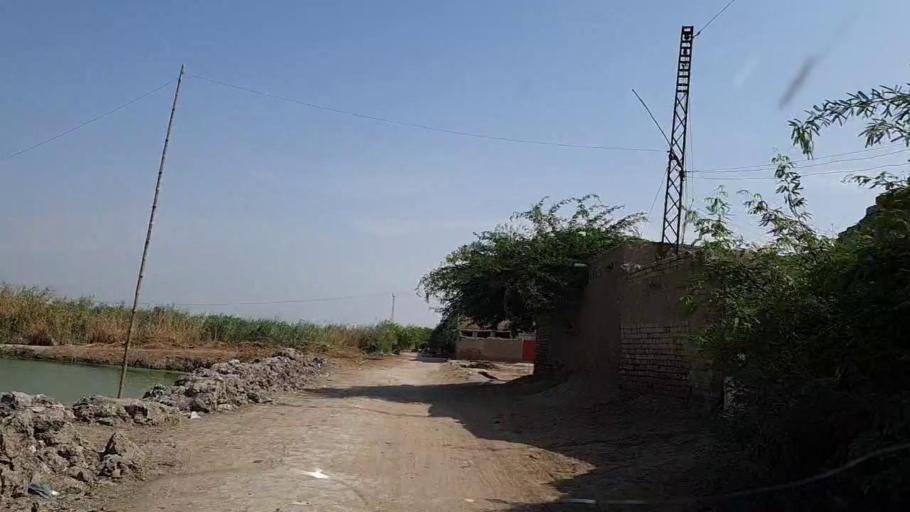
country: PK
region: Sindh
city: Khanpur
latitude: 27.7488
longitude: 69.3405
